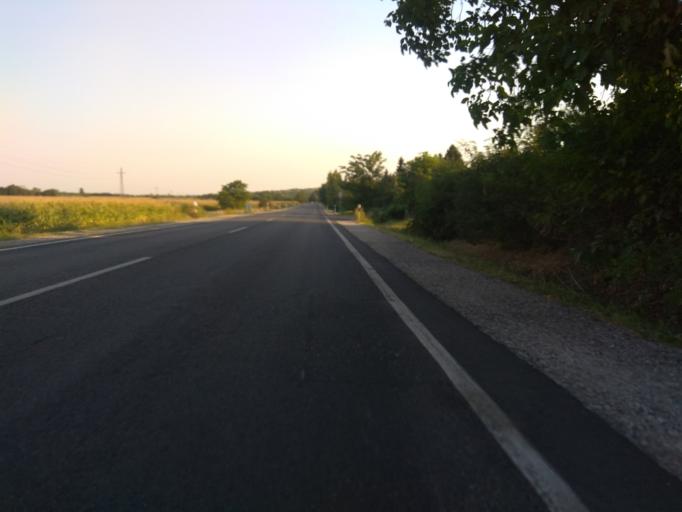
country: HU
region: Borsod-Abauj-Zemplen
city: Nyekladhaza
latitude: 47.9821
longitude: 20.8310
